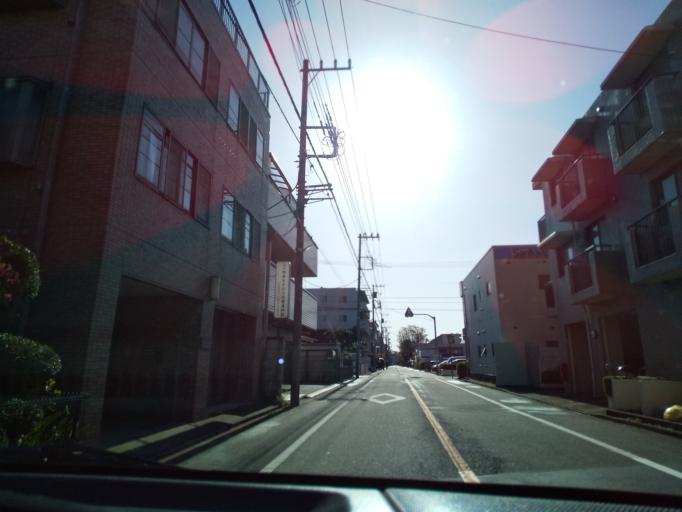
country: JP
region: Tokyo
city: Hino
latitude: 35.6863
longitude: 139.4338
